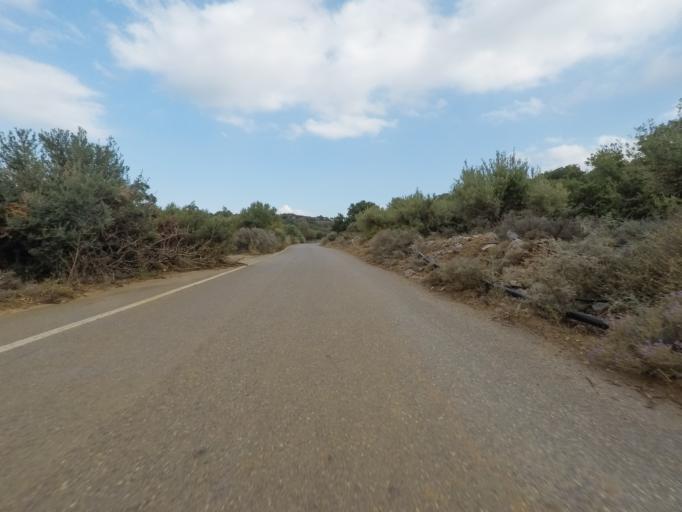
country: GR
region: Crete
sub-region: Nomos Lasithiou
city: Kritsa
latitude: 35.1703
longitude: 25.6539
